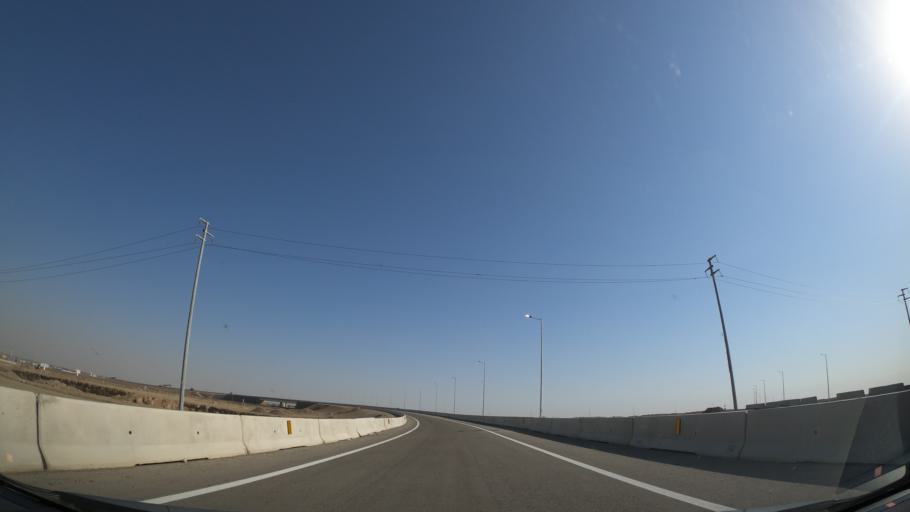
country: IR
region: Tehran
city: Eqbaliyeh
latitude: 35.1348
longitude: 51.5087
